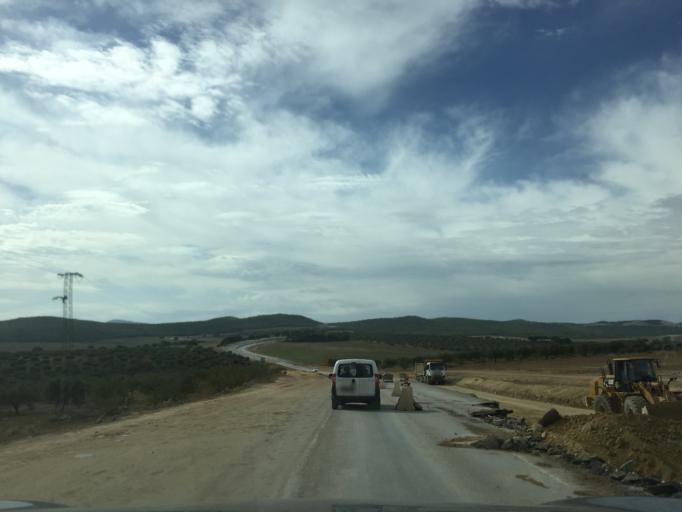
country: TN
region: Zaghwan
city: El Fahs
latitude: 36.2876
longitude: 9.8073
